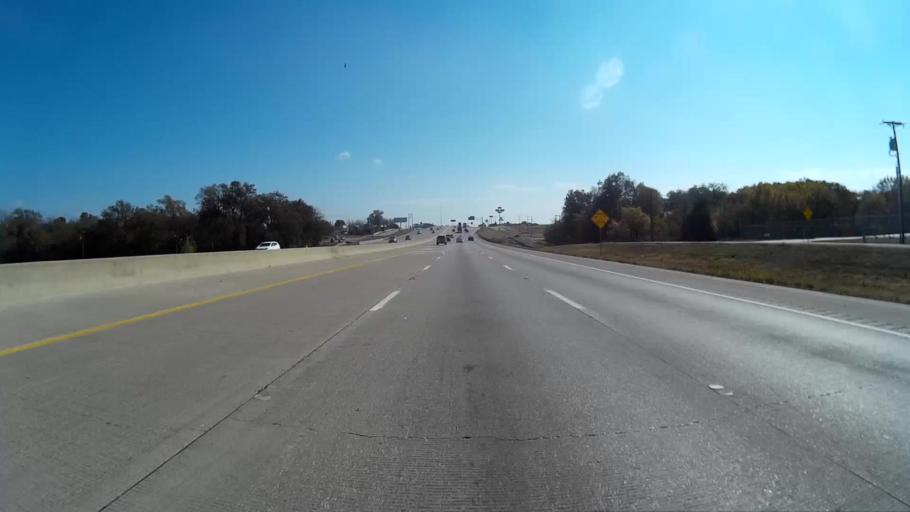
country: US
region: Texas
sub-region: Dallas County
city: Wilmer
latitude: 32.5980
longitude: -96.6829
